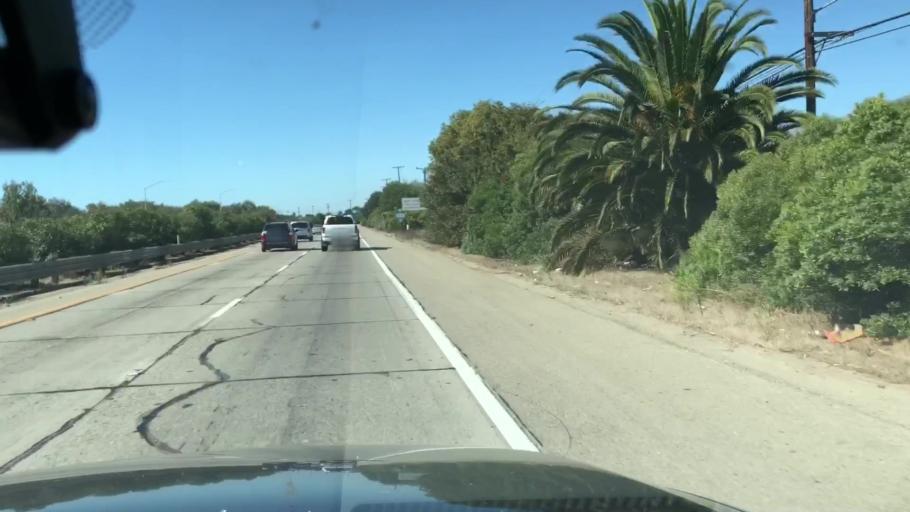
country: US
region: California
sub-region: Santa Barbara County
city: Carpinteria
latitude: 34.4052
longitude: -119.5360
